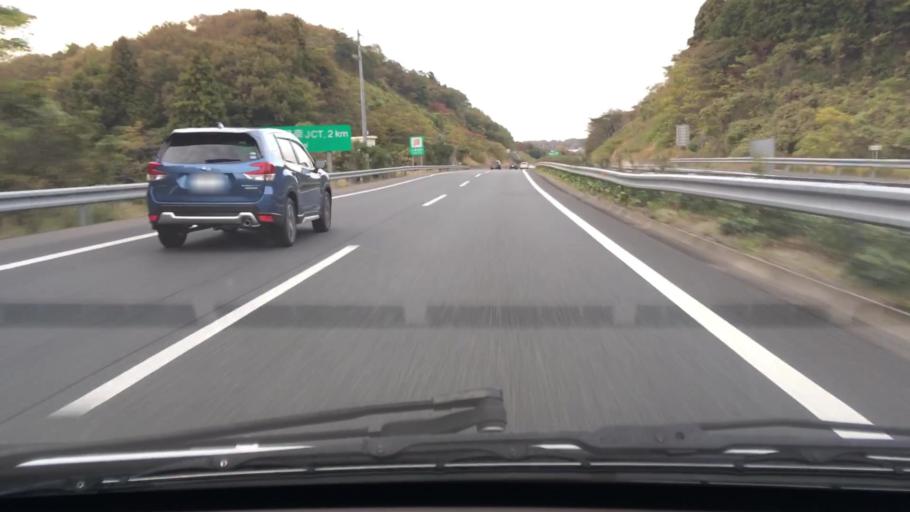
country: JP
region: Chiba
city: Kisarazu
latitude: 35.3338
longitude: 139.9452
